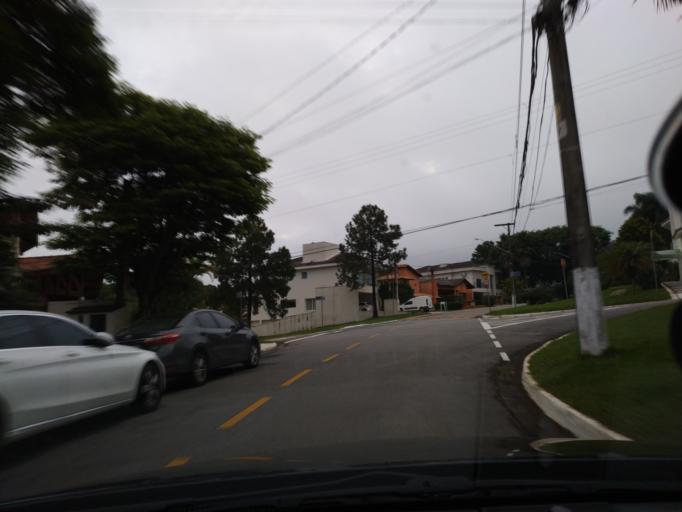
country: BR
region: Sao Paulo
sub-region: Santana De Parnaiba
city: Santana de Parnaiba
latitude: -23.4514
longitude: -46.8875
